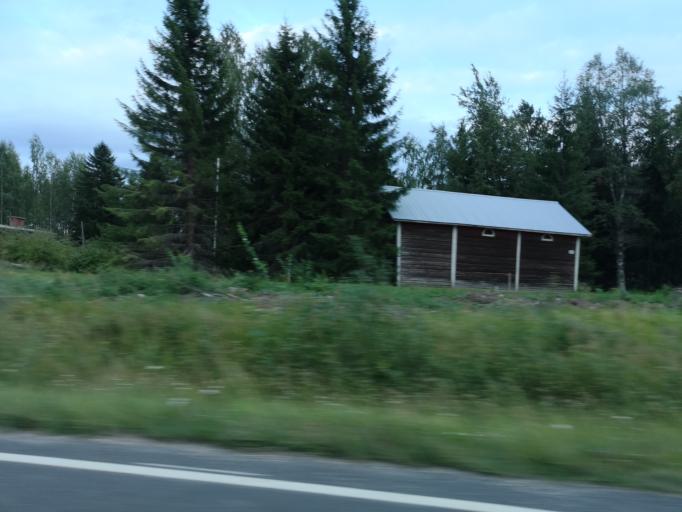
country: FI
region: Central Finland
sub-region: Joutsa
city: Leivonmaeki
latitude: 61.8741
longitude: 26.1080
